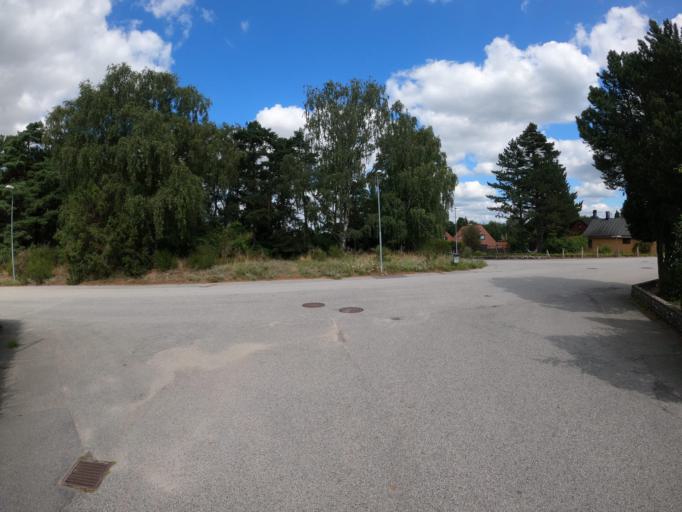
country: SE
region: Skane
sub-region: Lunds Kommun
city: Genarp
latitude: 55.5966
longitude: 13.3991
